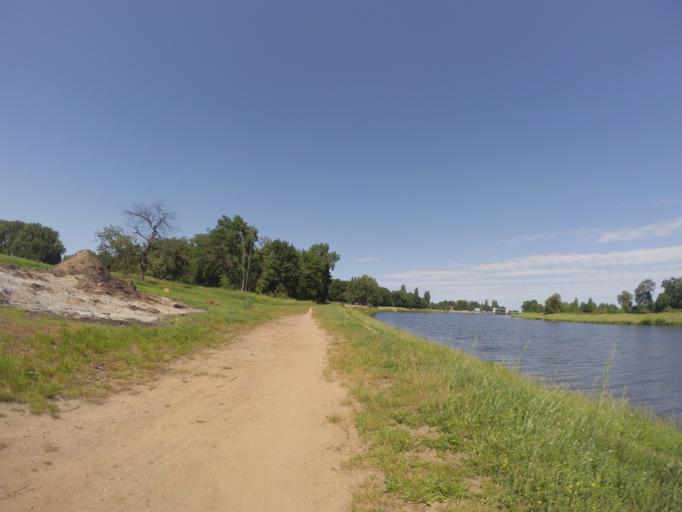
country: CZ
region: Central Bohemia
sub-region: Okres Nymburk
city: Sadska
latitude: 50.1662
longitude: 14.9771
